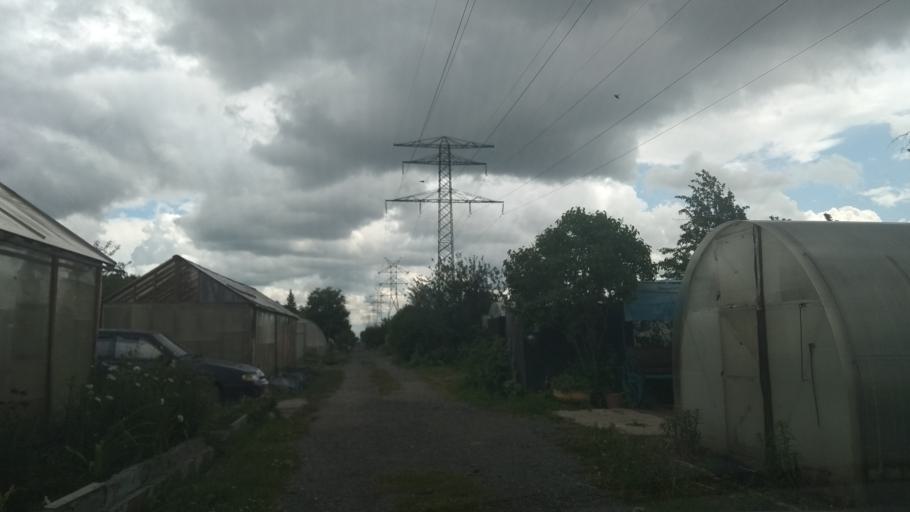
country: RU
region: Sverdlovsk
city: Verkhnyaya Pyshma
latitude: 56.9210
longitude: 60.5724
